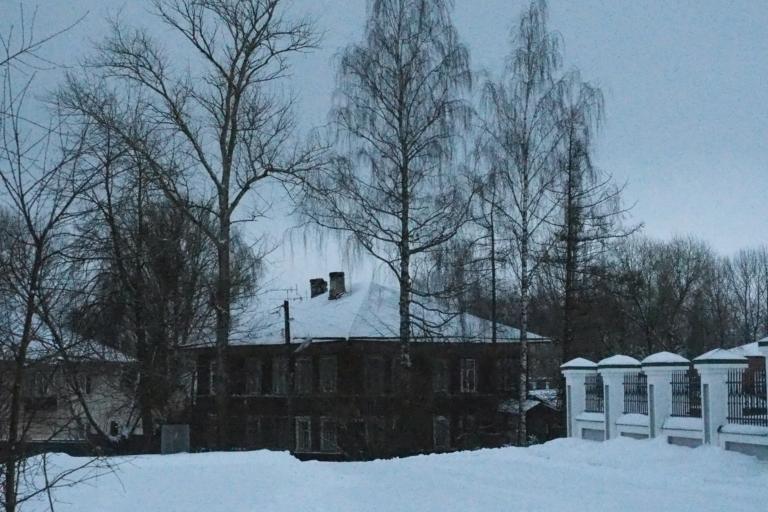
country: RU
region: Tverskaya
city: Bezhetsk
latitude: 57.7775
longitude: 36.7034
